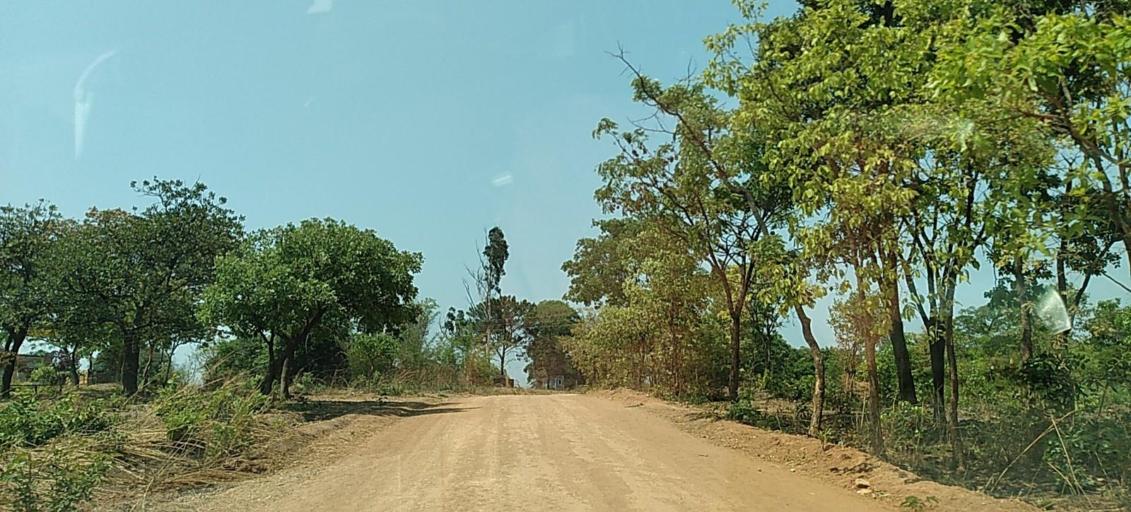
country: ZM
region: Copperbelt
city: Chambishi
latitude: -12.6202
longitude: 27.9553
